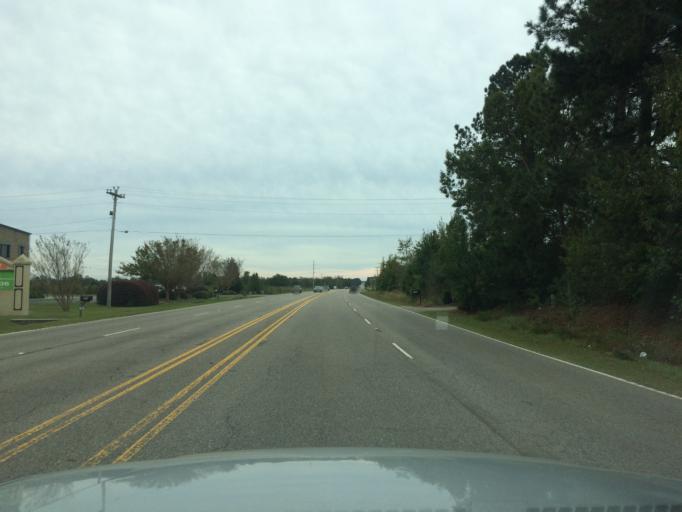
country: US
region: South Carolina
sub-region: Aiken County
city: New Ellenton
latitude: 33.4615
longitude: -81.6873
